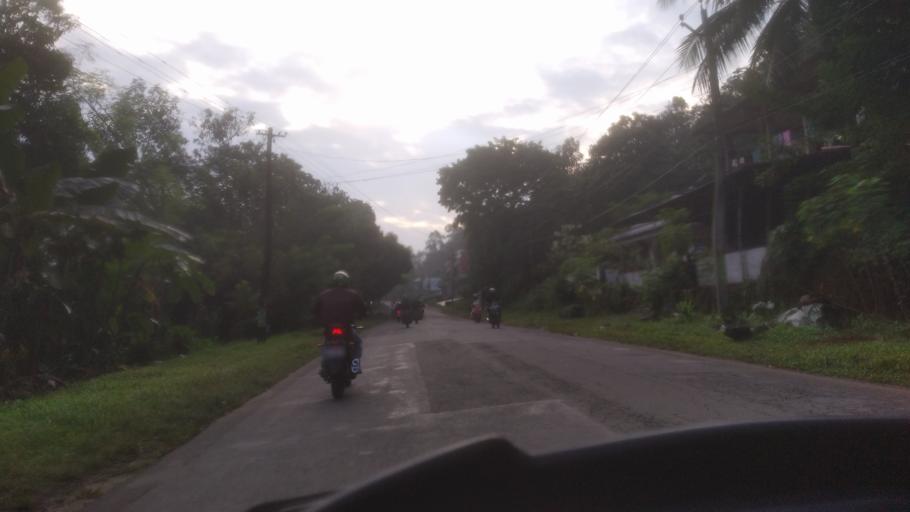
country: IN
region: Kerala
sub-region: Ernakulam
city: Perumpavur
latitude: 10.0985
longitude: 76.5478
